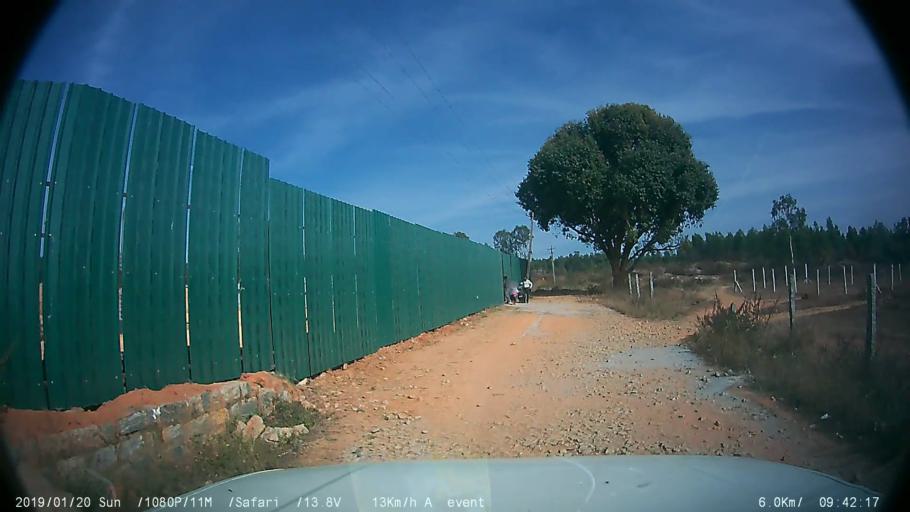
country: IN
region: Karnataka
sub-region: Bangalore Urban
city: Anekal
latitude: 12.8304
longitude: 77.6191
